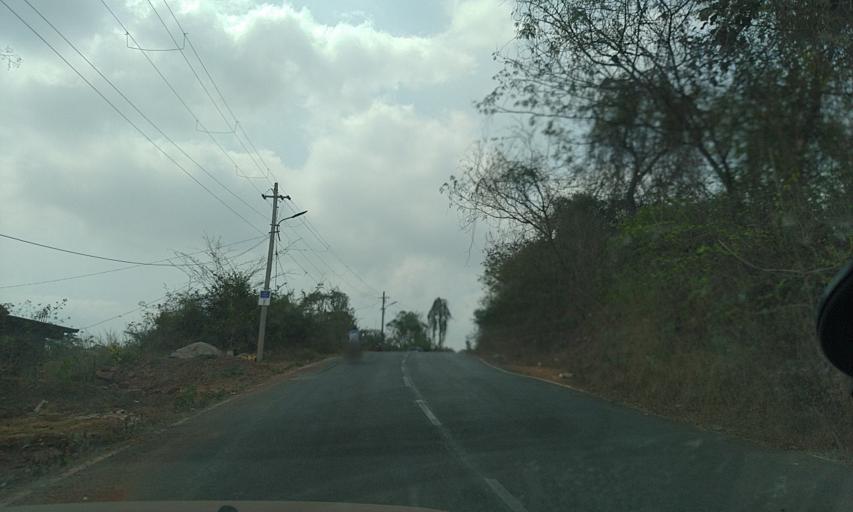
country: IN
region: Goa
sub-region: North Goa
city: Goa Velha
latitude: 15.4907
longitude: 73.9111
